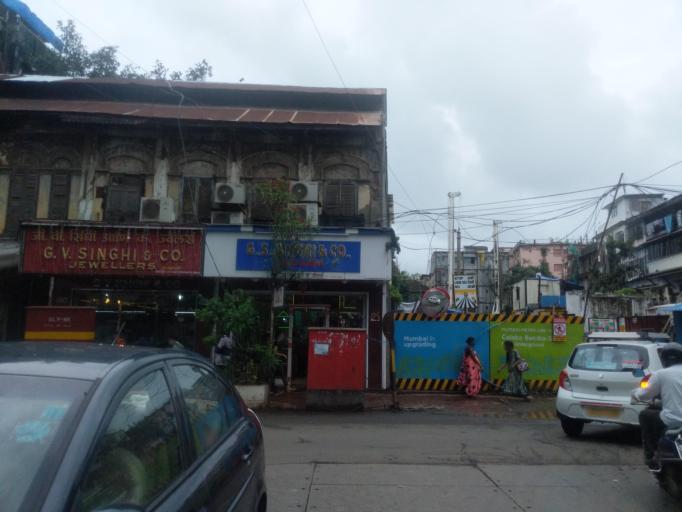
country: IN
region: Maharashtra
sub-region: Raigarh
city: Uran
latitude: 18.9472
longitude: 72.8267
